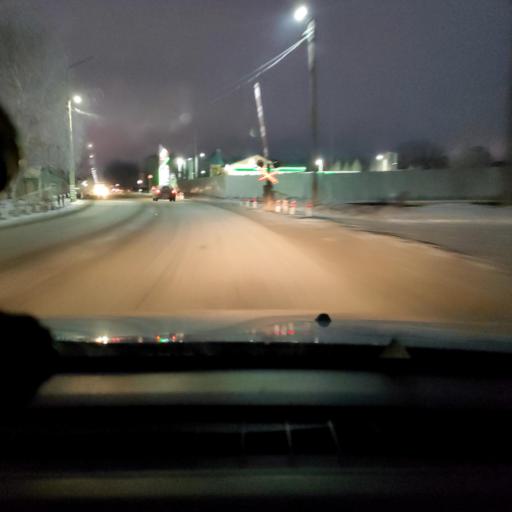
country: RU
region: Samara
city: Chapayevsk
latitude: 52.9690
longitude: 49.6966
